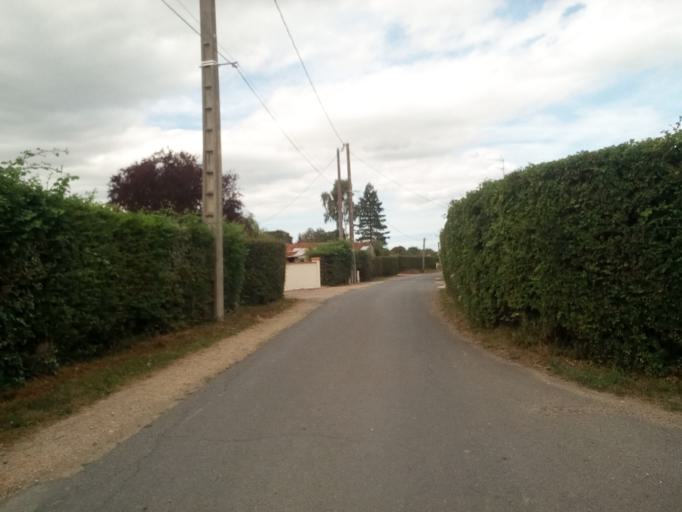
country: FR
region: Lower Normandy
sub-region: Departement du Calvados
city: Troarn
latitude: 49.1610
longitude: -0.1604
